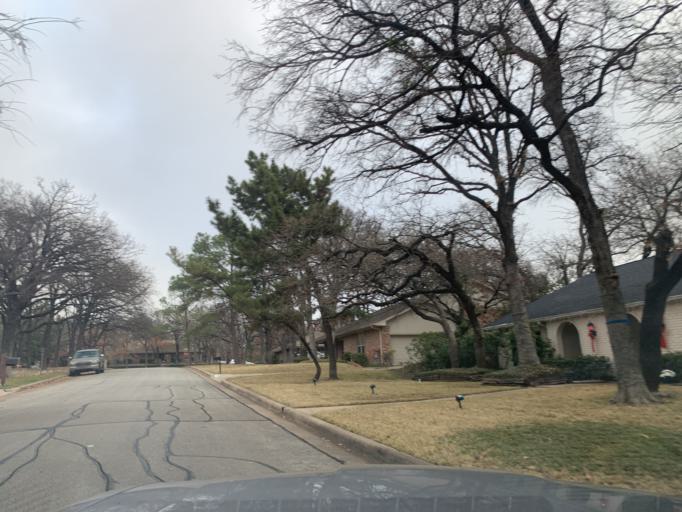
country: US
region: Texas
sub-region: Tarrant County
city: Bedford
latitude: 32.8299
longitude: -97.1478
